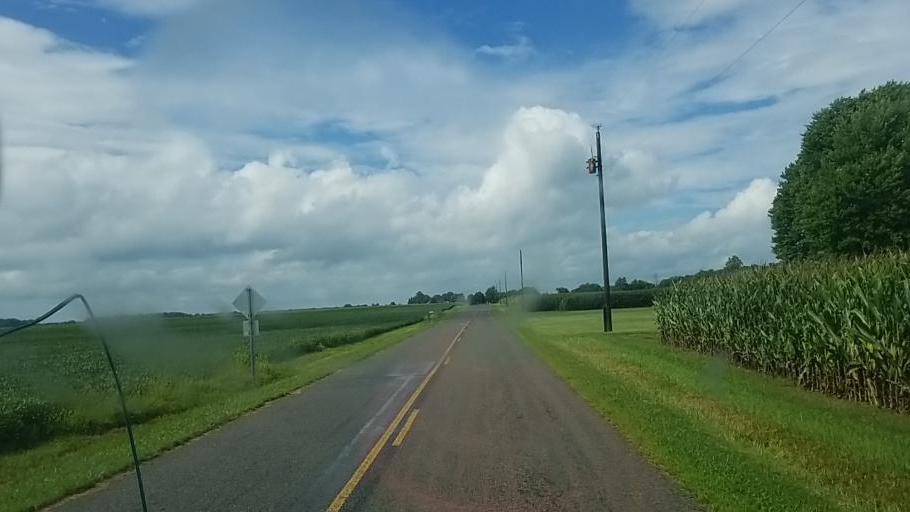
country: US
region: Ohio
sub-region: Hardin County
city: Kenton
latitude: 40.4713
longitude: -83.5089
